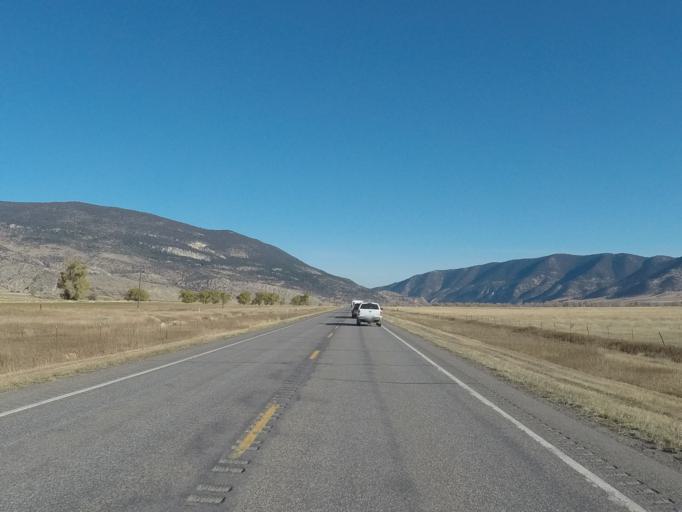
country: US
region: Montana
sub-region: Park County
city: Livingston
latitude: 45.5450
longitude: -110.5995
